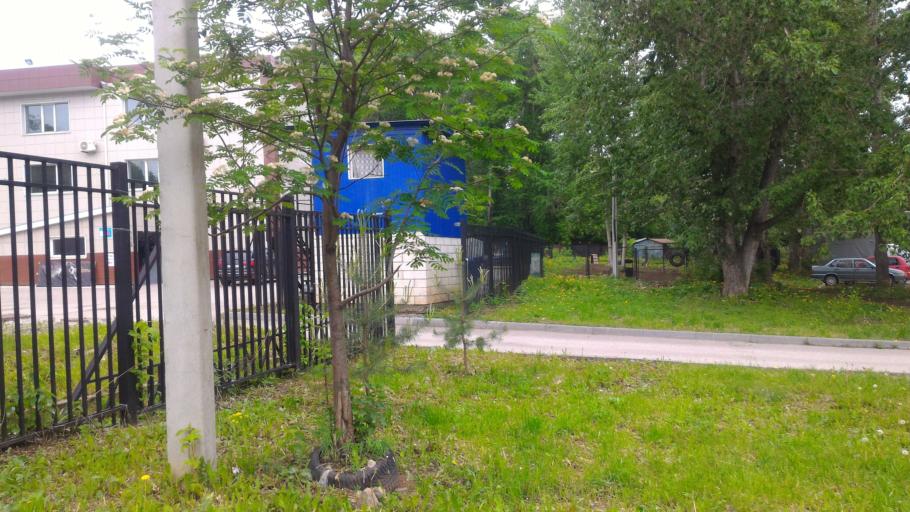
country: RU
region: Perm
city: Perm
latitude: 57.9913
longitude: 56.2272
